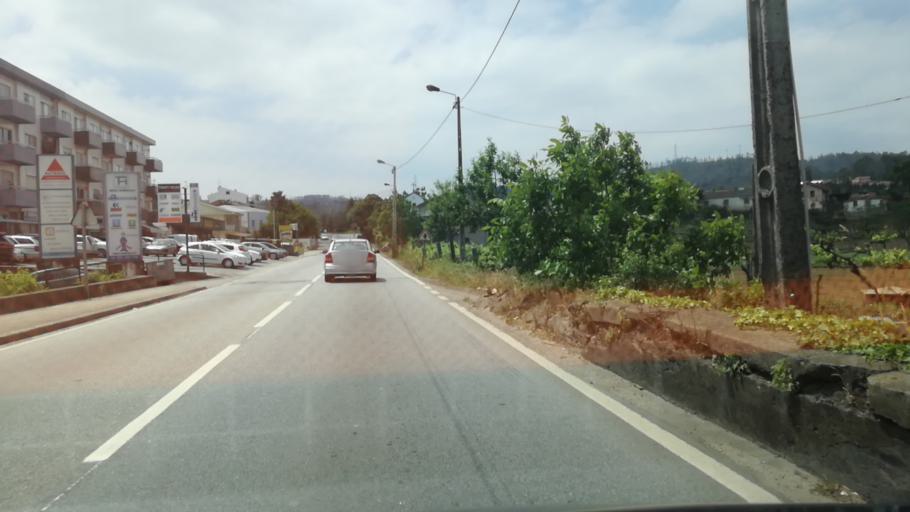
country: PT
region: Porto
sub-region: Trofa
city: Bougado
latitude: 41.3211
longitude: -8.5734
